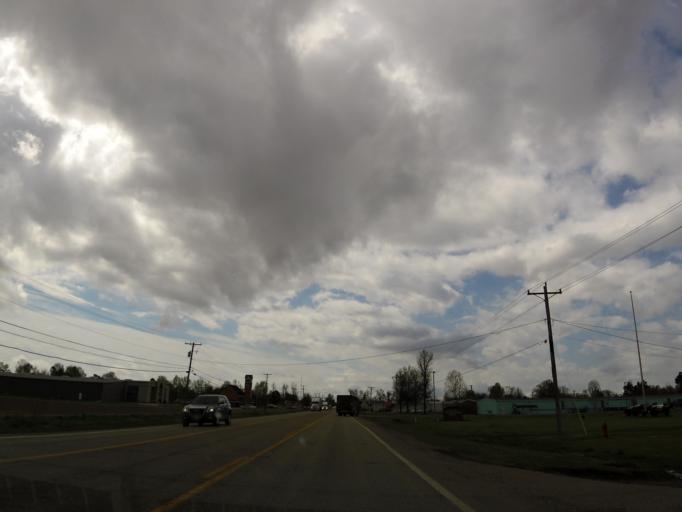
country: US
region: Arkansas
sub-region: Clay County
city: Corning
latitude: 36.4208
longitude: -90.5862
